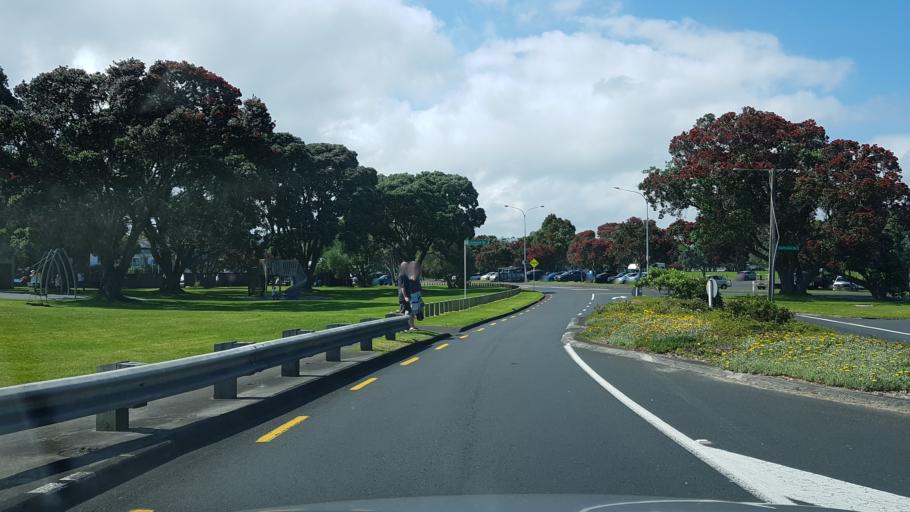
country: NZ
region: Auckland
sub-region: Auckland
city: North Shore
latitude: -36.8125
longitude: 174.8009
